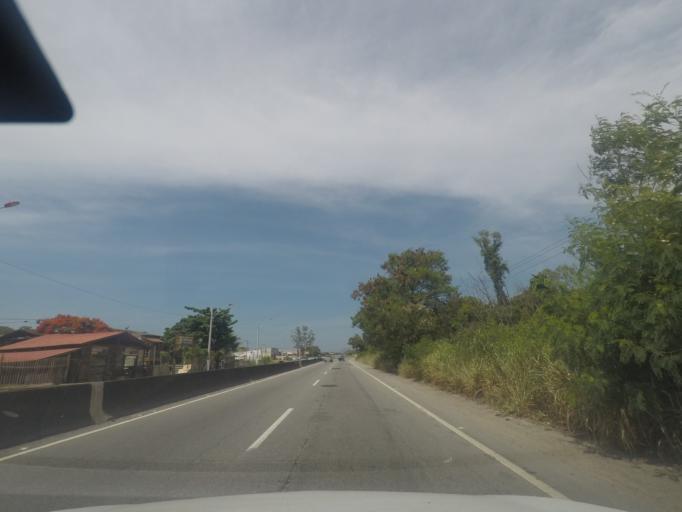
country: BR
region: Rio de Janeiro
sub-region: Marica
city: Marica
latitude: -22.9112
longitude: -42.8422
